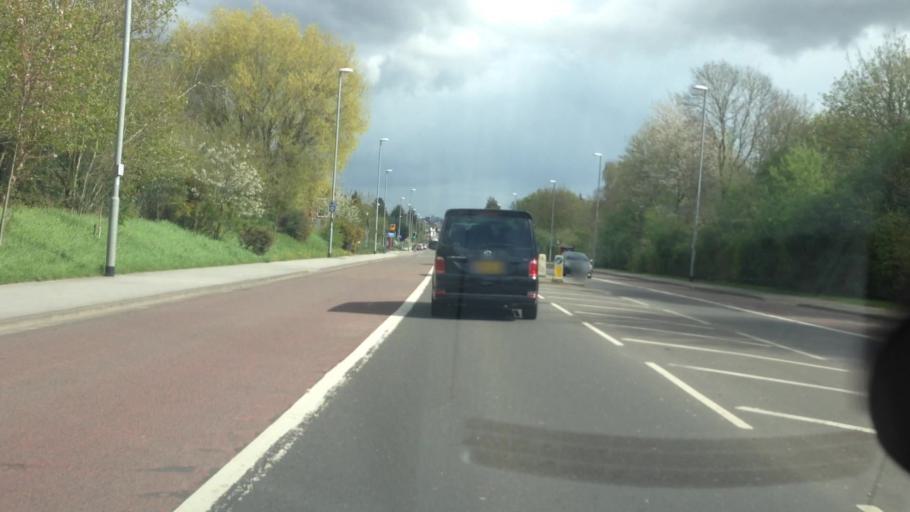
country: GB
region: England
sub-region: City and Borough of Leeds
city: Horsforth
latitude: 53.8114
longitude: -1.5968
